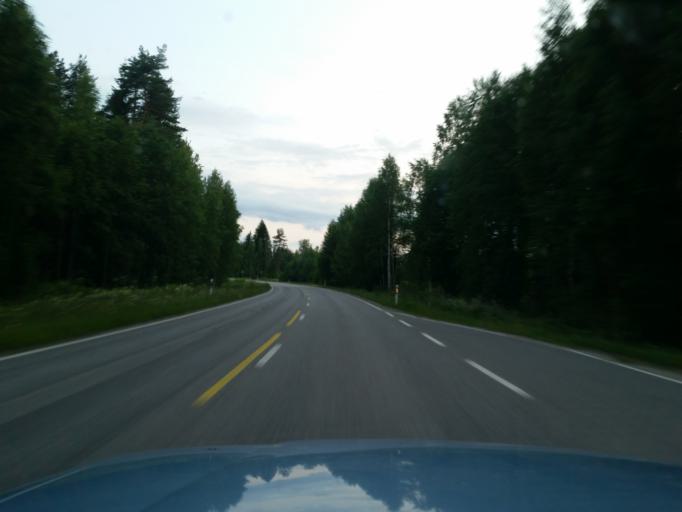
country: FI
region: Southern Savonia
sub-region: Savonlinna
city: Sulkava
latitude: 61.8315
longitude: 28.4493
